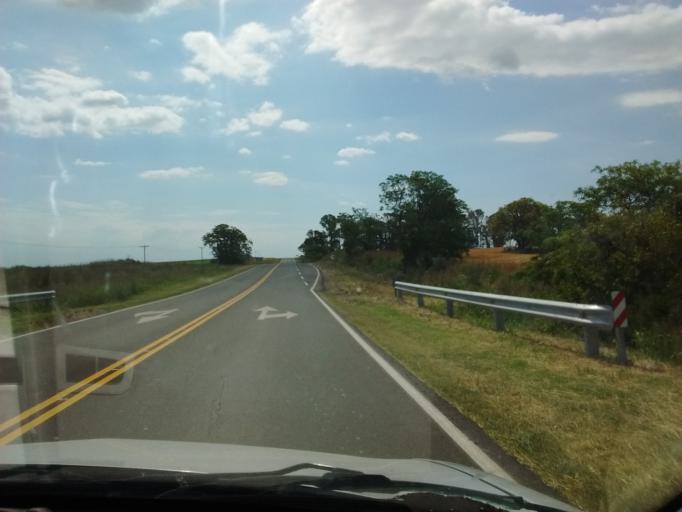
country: AR
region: Entre Rios
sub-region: Departamento de Victoria
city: Victoria
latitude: -32.6566
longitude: -60.0638
